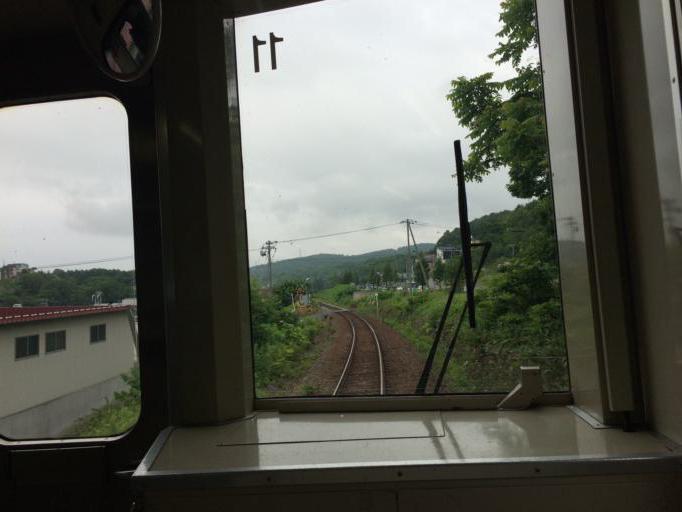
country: JP
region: Hokkaido
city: Otaru
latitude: 43.2146
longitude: 140.9584
